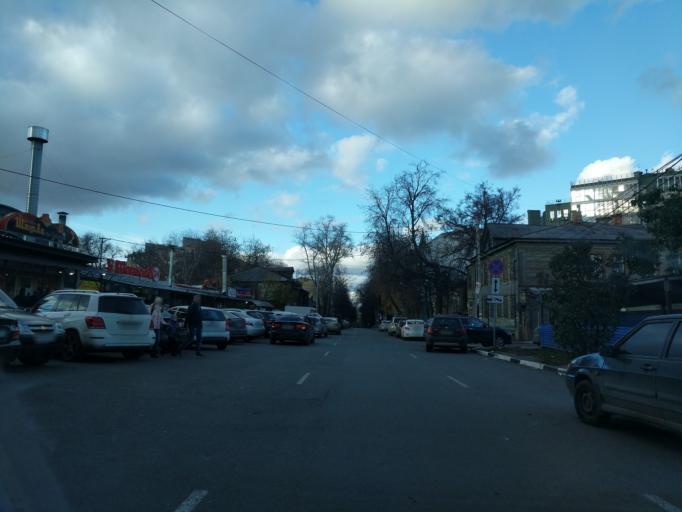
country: RU
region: Nizjnij Novgorod
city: Nizhniy Novgorod
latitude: 56.3094
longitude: 43.9914
